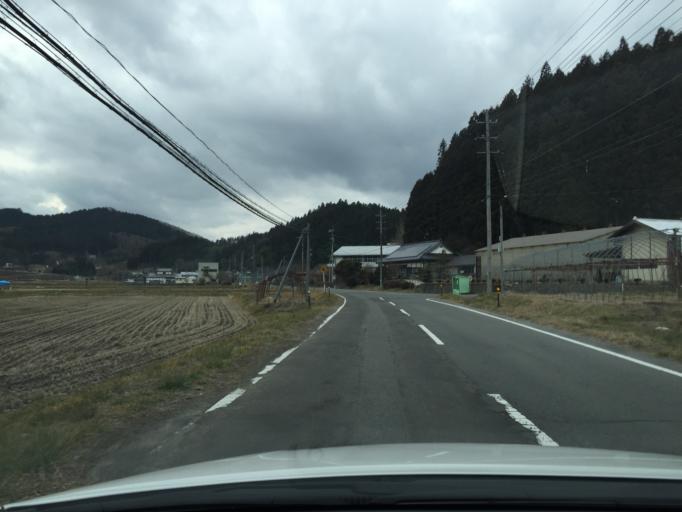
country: JP
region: Fukushima
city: Ishikawa
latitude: 37.1997
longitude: 140.6401
